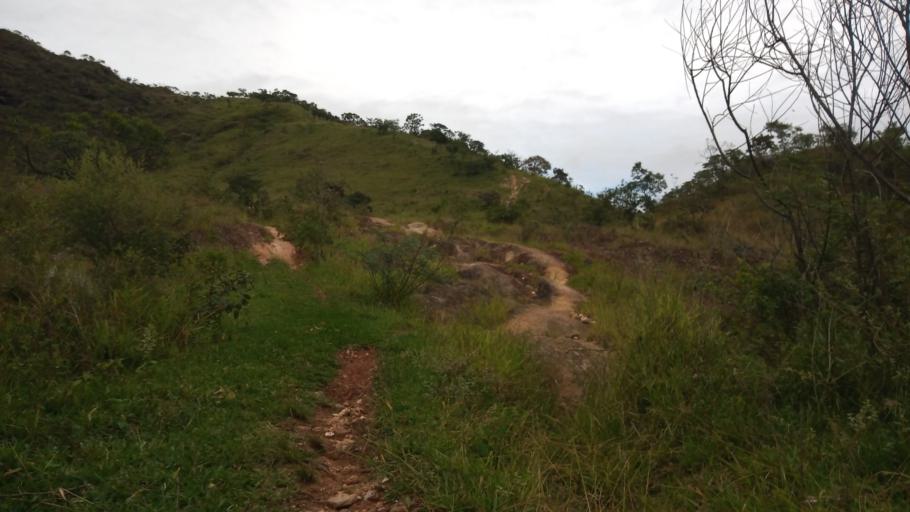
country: BR
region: Minas Gerais
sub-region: Sao Joao Del Rei
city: Sao Joao del Rei
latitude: -21.1261
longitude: -44.2722
